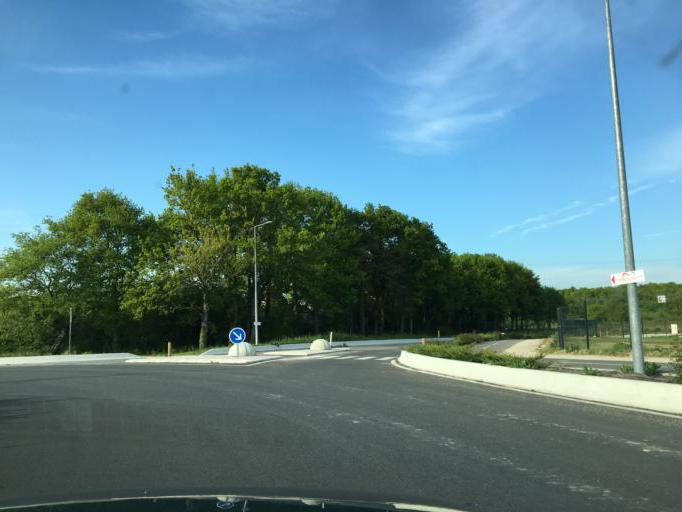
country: FR
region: Centre
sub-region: Departement du Loiret
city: Ingre
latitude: 47.9340
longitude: 1.8441
